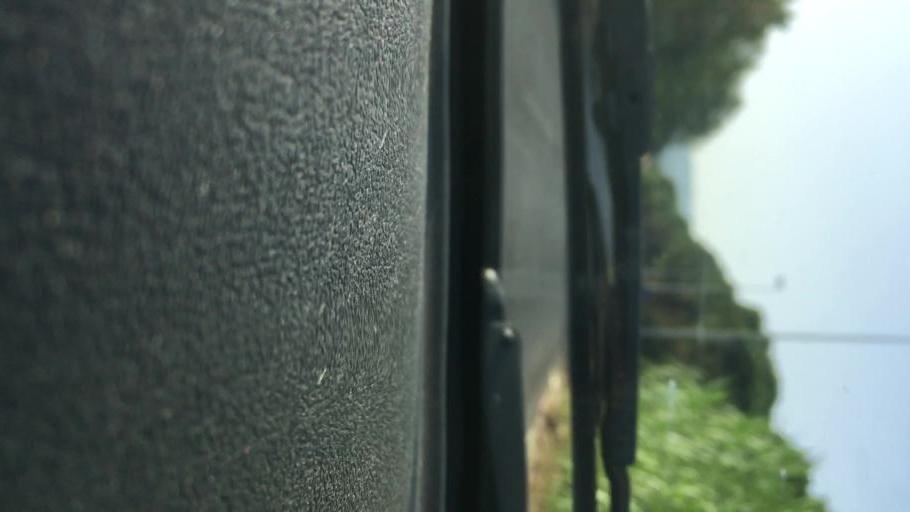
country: IT
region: Latium
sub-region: Citta metropolitana di Roma Capitale
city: Ciampino
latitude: 41.8292
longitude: 12.6214
